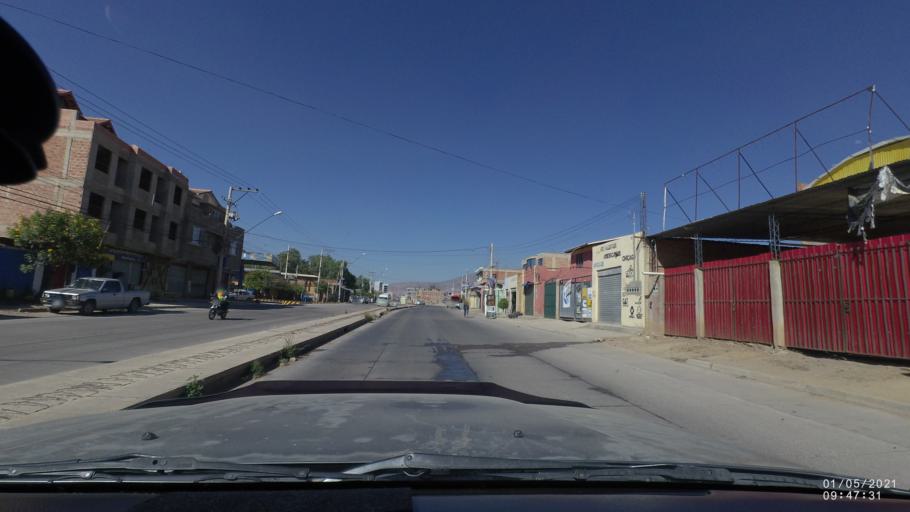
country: BO
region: Cochabamba
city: Cochabamba
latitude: -17.4464
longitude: -66.1651
